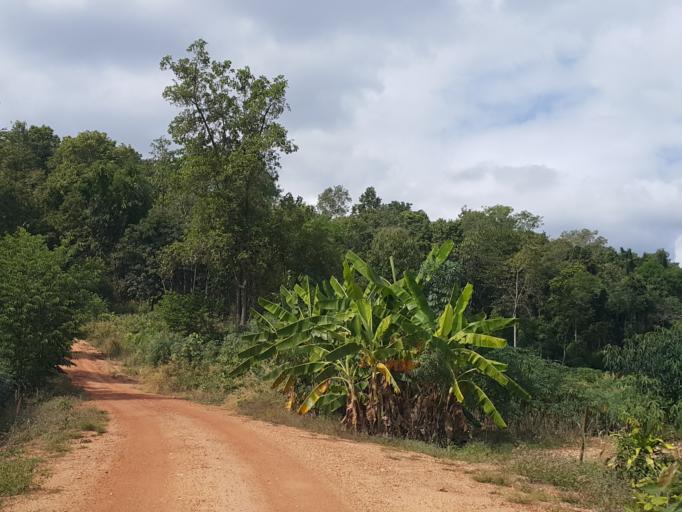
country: TH
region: Lampang
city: Hang Chat
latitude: 18.4911
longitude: 99.4009
